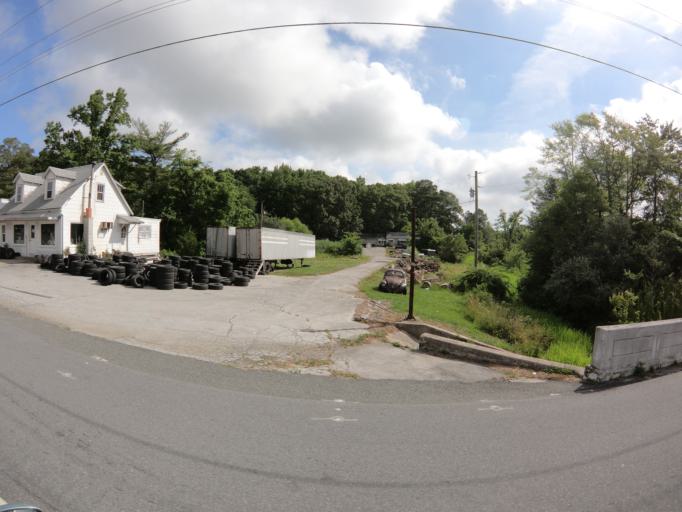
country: US
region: Delaware
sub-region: Sussex County
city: Lewes
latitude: 38.7612
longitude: -75.2044
